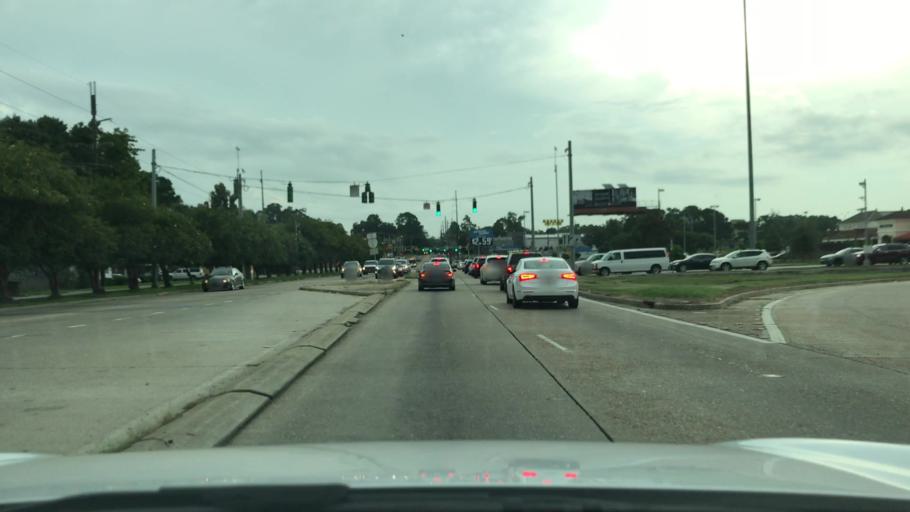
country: US
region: Louisiana
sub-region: East Baton Rouge Parish
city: Baton Rouge
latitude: 30.4238
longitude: -91.1389
